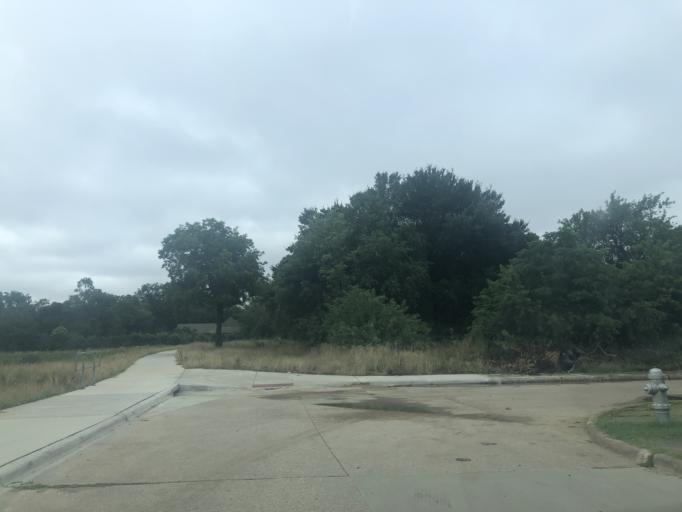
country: US
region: Texas
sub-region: Dallas County
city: Dallas
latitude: 32.7870
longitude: -96.8421
